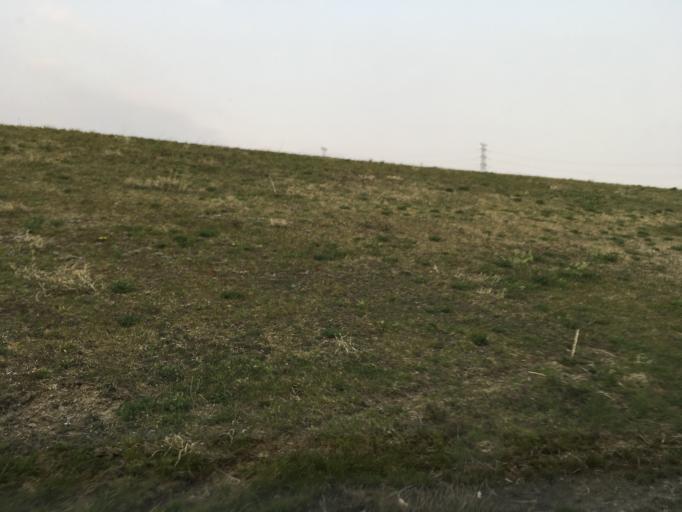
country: JP
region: Iwate
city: Ichinoseki
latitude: 38.9424
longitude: 141.2462
